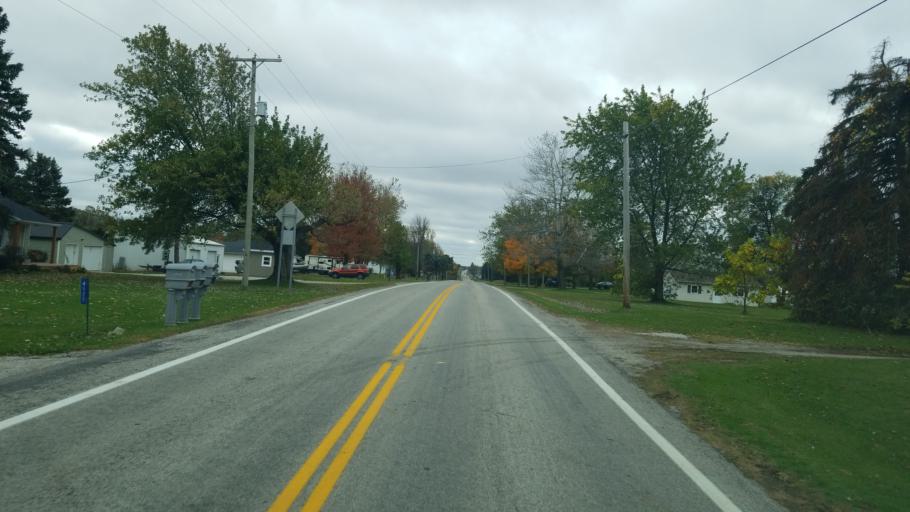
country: US
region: Ohio
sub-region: Crawford County
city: Crestline
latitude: 40.8691
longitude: -82.7740
